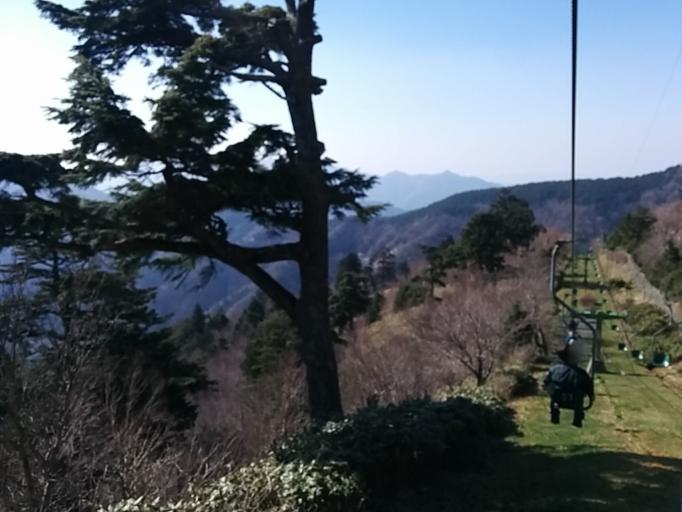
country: JP
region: Tokushima
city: Wakimachi
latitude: 33.8618
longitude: 134.0916
